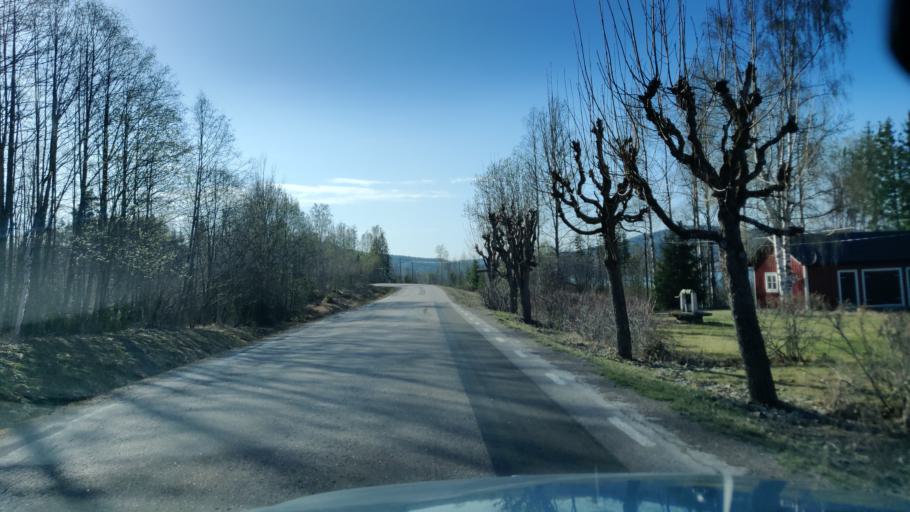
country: SE
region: Vaermland
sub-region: Munkfors Kommun
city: Munkfors
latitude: 59.9703
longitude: 13.4567
